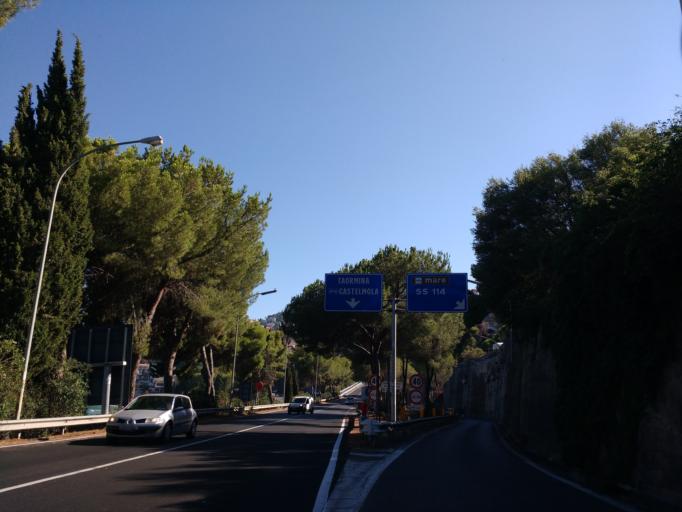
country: IT
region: Sicily
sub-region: Messina
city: Taormina
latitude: 37.8656
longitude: 15.2964
